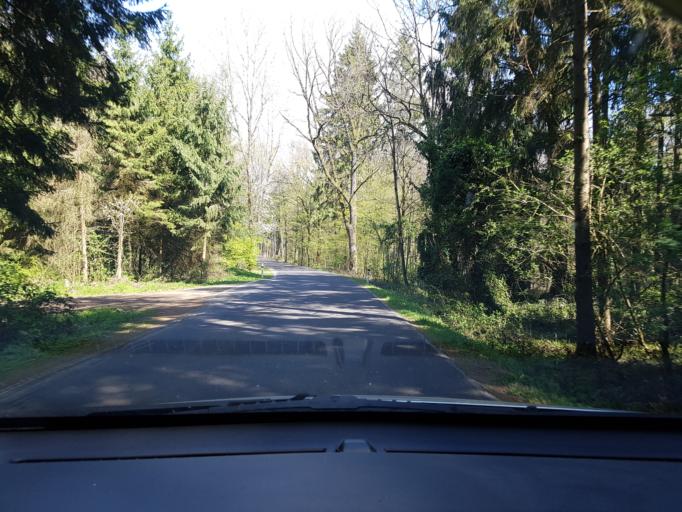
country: AT
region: Upper Austria
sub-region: Politischer Bezirk Linz-Land
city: Sankt Florian
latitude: 48.2065
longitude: 14.3427
